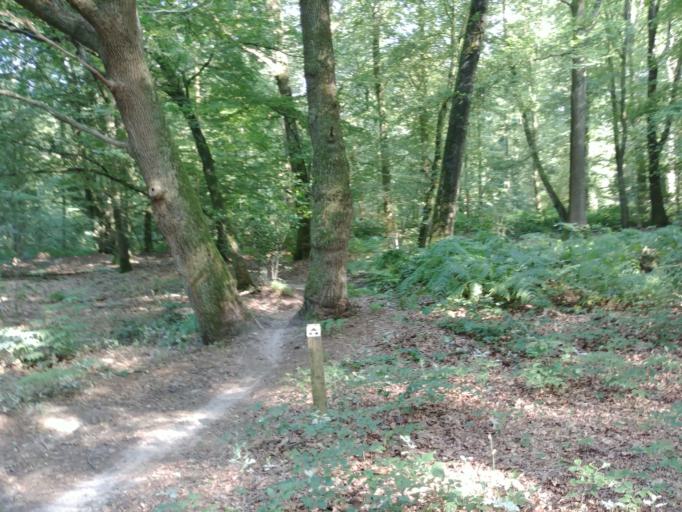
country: NL
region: Gelderland
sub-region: Gemeente Renkum
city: Doorwerth
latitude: 51.9732
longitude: 5.8019
